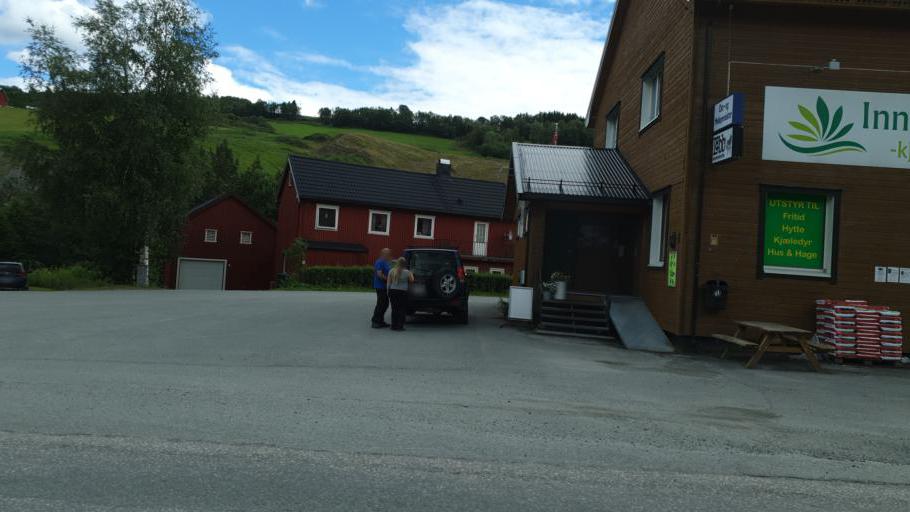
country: NO
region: Sor-Trondelag
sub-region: Midtre Gauldal
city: Storen
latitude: 62.9506
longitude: 10.1891
